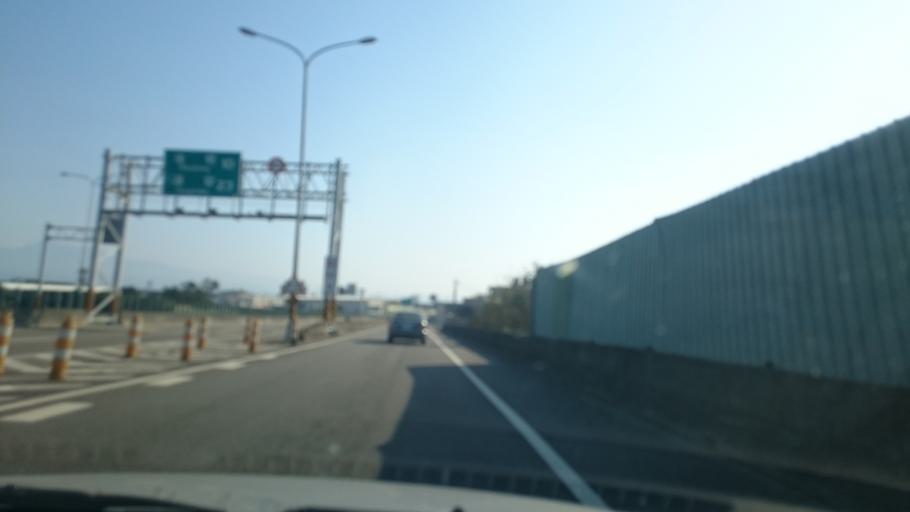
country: TW
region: Taiwan
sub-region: Hsinchu
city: Hsinchu
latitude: 24.7085
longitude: 120.8672
